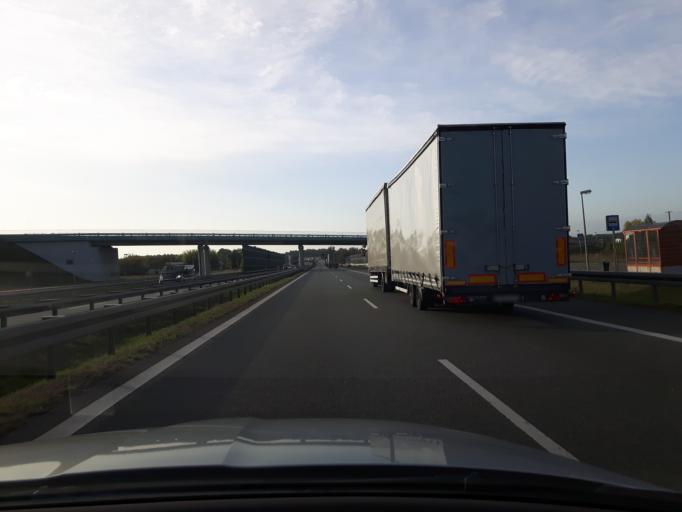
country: PL
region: Masovian Voivodeship
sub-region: Powiat bialobrzeski
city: Stara Blotnica
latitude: 51.5852
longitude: 20.9990
